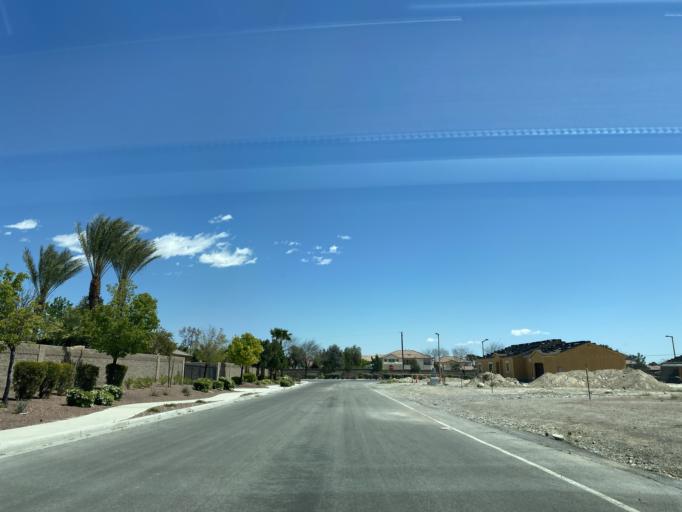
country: US
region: Nevada
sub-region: Clark County
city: North Las Vegas
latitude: 36.3107
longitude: -115.2257
